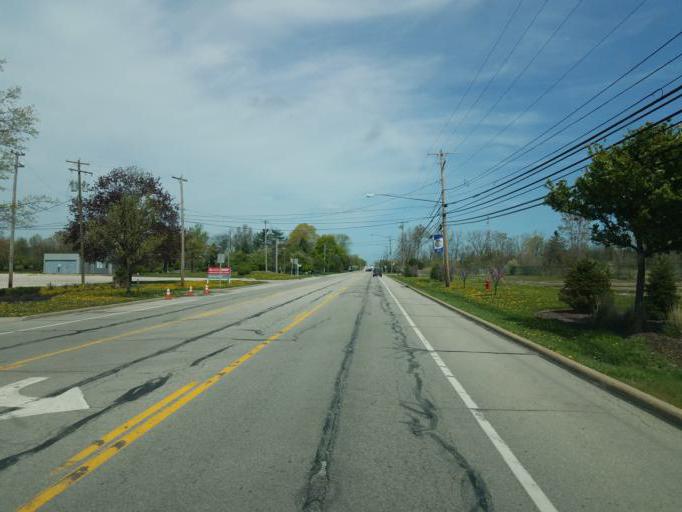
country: US
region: Ohio
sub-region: Summit County
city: Richfield
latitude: 41.2068
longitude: -81.6380
